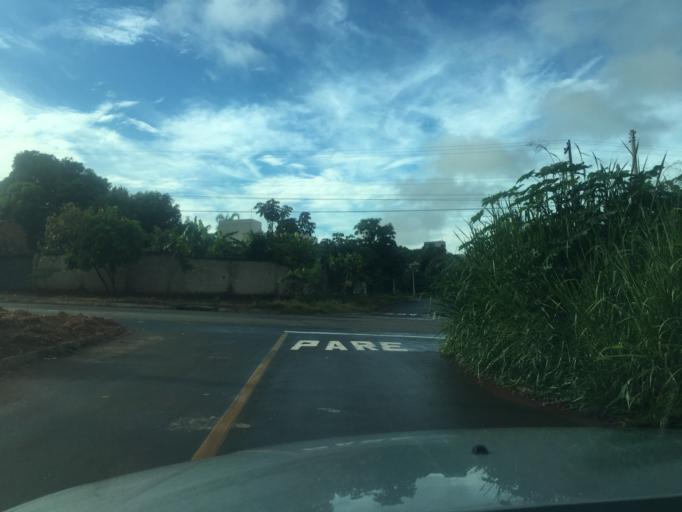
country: BR
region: Goias
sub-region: Aparecida De Goiania
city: Aparecida de Goiania
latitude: -16.8030
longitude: -49.2458
